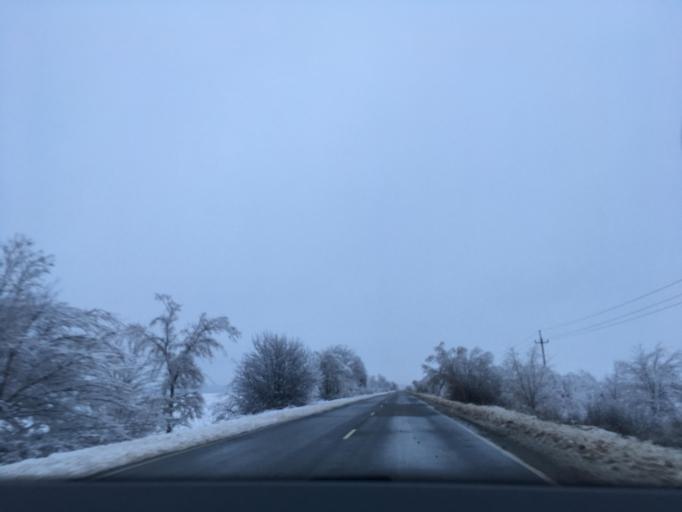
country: RU
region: Voronezj
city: Verkhniy Mamon
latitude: 50.0215
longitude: 40.0979
